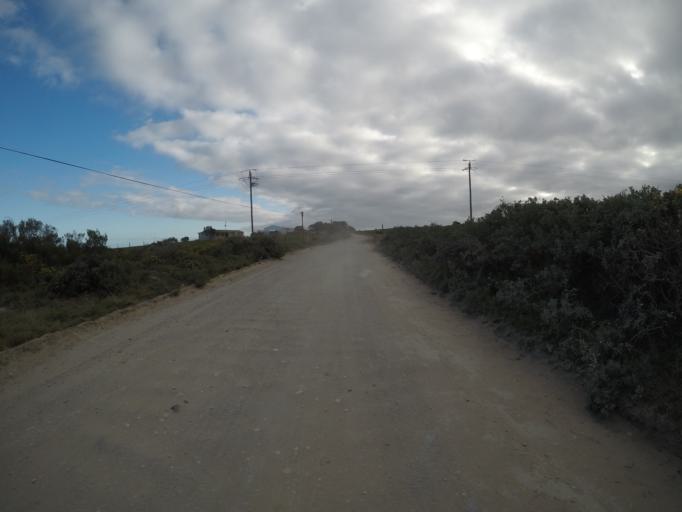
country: ZA
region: Western Cape
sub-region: Eden District Municipality
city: Riversdale
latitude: -34.4184
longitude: 21.3414
